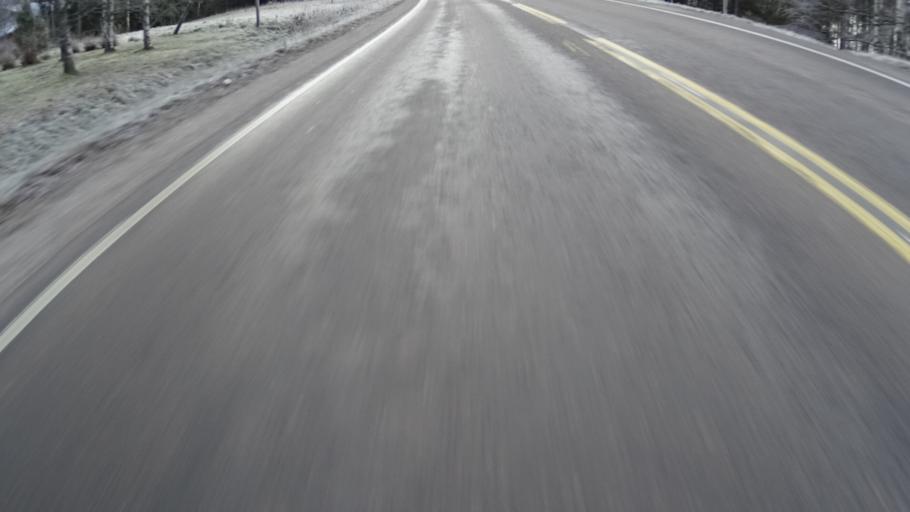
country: FI
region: Uusimaa
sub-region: Helsinki
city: Nurmijaervi
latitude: 60.4046
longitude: 24.7311
